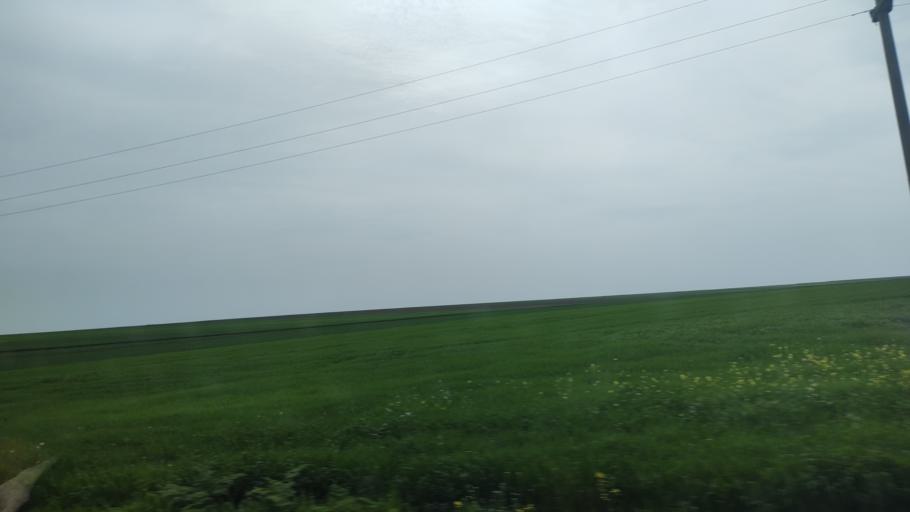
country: RO
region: Constanta
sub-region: Comuna Ciocarlia
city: Ciocarlia
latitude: 44.1075
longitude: 28.3017
